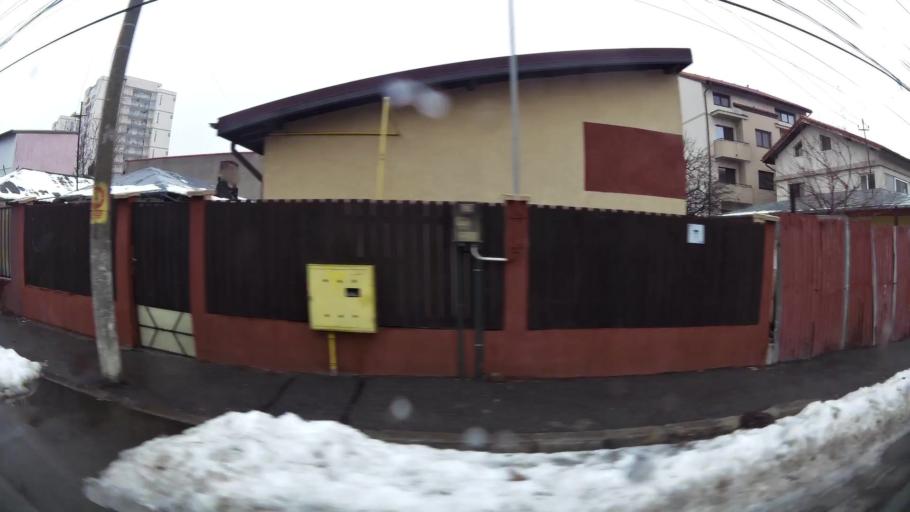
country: RO
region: Ilfov
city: Dobroesti
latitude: 44.4206
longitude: 26.1831
